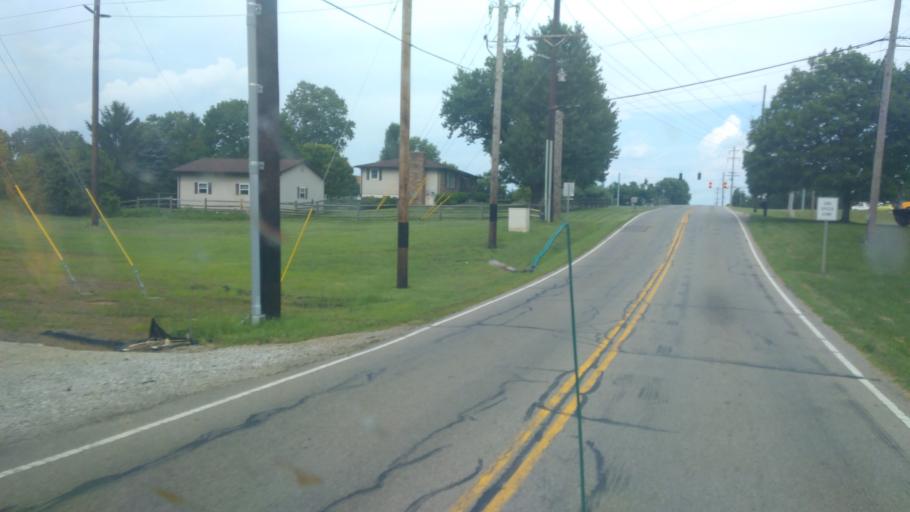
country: US
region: Ohio
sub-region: Fairfield County
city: Lancaster
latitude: 39.7678
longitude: -82.5787
